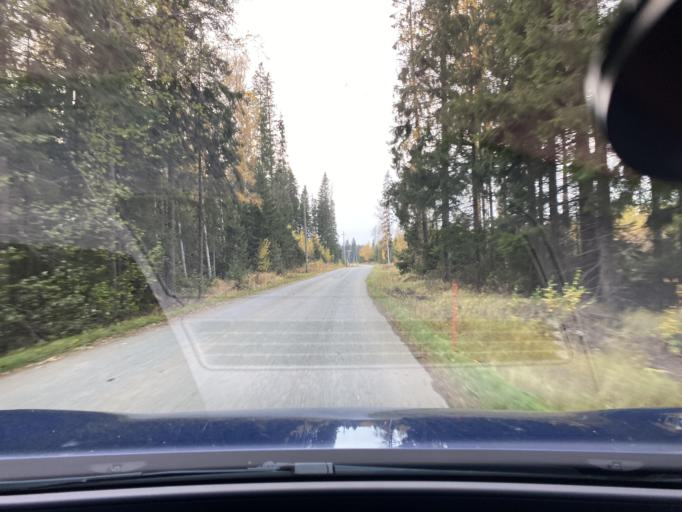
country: FI
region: Varsinais-Suomi
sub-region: Loimaa
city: Alastaro
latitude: 61.0816
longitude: 22.9440
